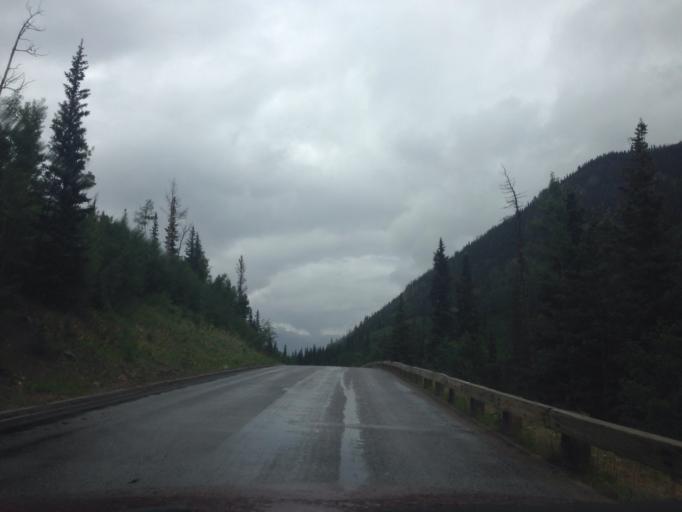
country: US
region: Colorado
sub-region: Clear Creek County
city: Georgetown
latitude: 39.6424
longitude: -105.7078
